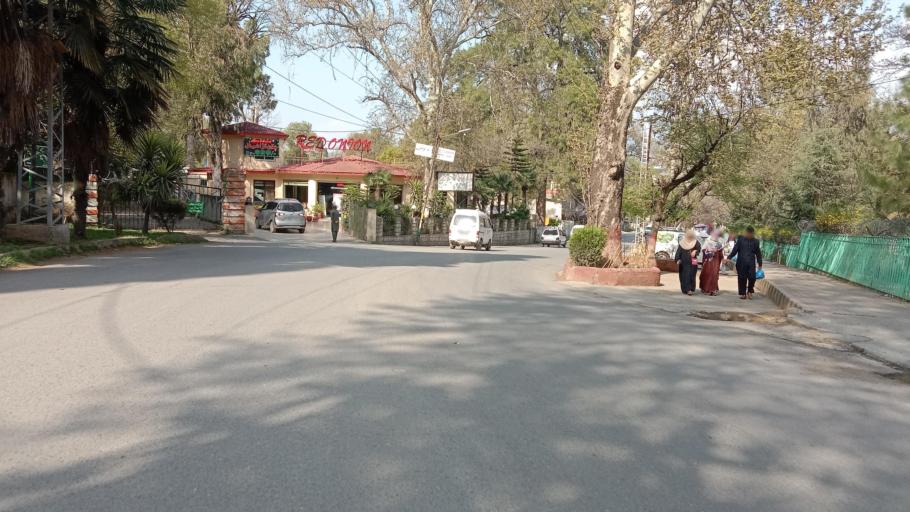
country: PK
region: Khyber Pakhtunkhwa
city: Abbottabad
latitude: 34.1496
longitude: 73.2140
